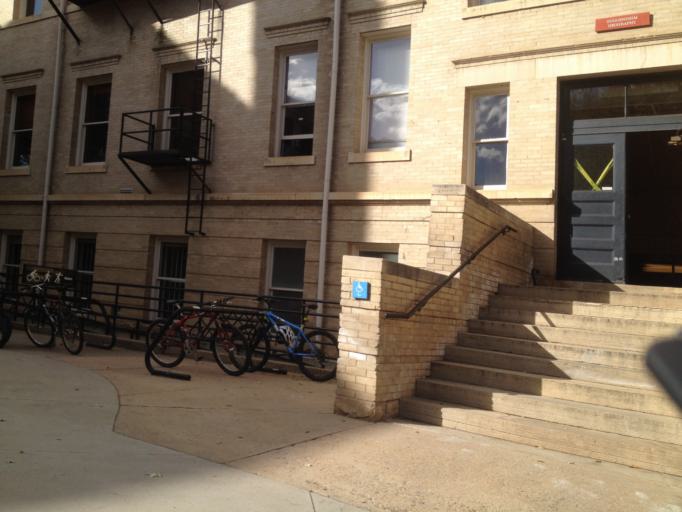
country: US
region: Colorado
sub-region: Boulder County
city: Boulder
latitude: 40.0079
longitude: -105.2743
